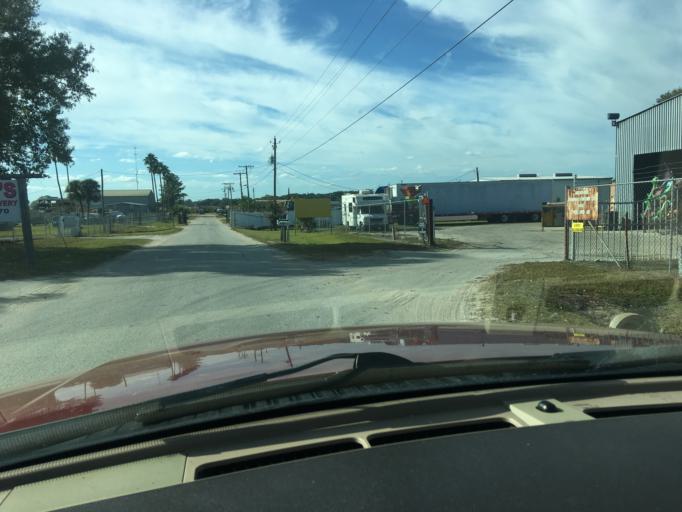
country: US
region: Florida
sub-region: Polk County
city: Mulberry
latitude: 27.9113
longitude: -81.9799
